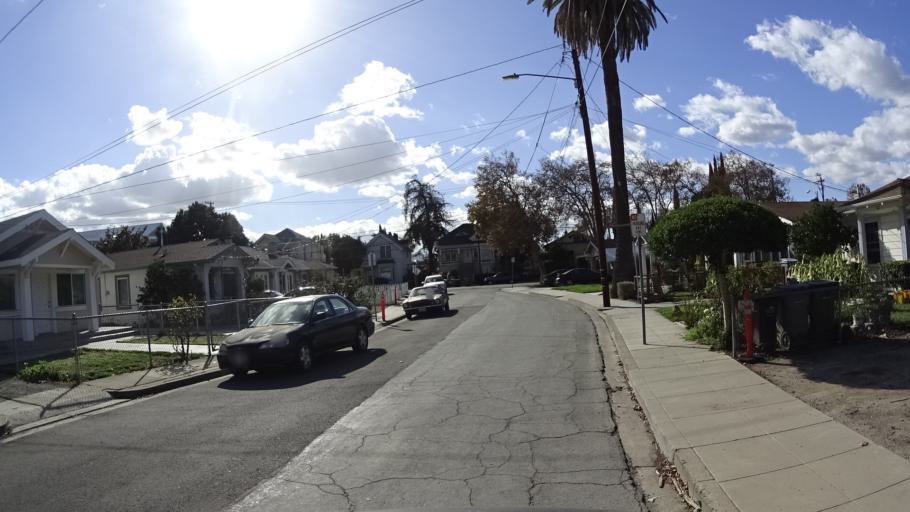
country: US
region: California
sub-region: Santa Clara County
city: San Jose
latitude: 37.3356
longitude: -121.9011
